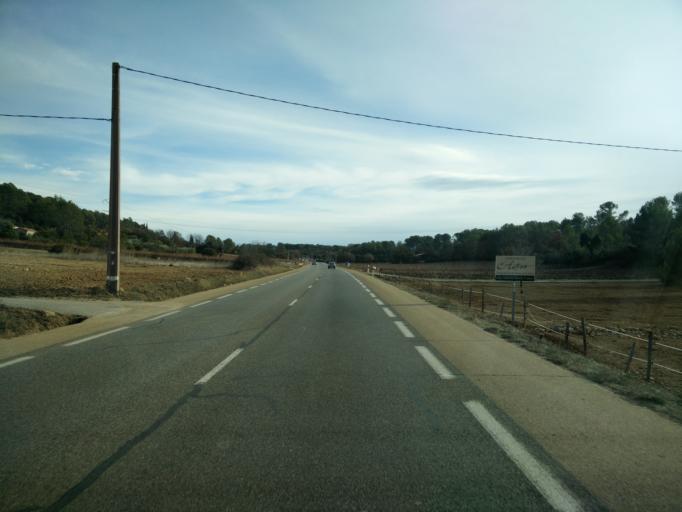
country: FR
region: Provence-Alpes-Cote d'Azur
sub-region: Departement du Var
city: Lorgues
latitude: 43.4703
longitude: 6.3819
